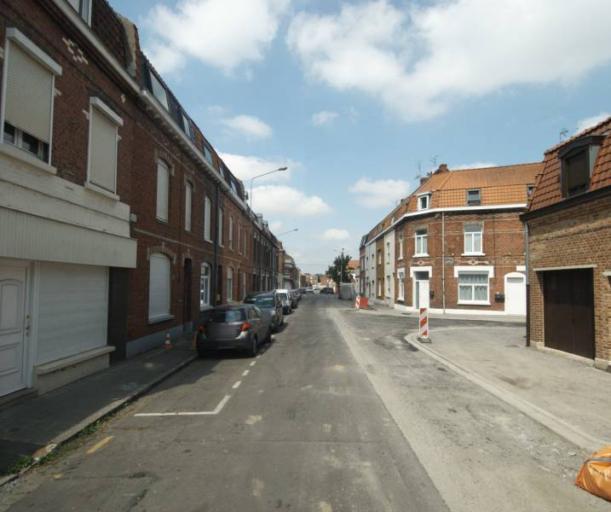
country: FR
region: Nord-Pas-de-Calais
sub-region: Departement du Nord
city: Armentieres
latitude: 50.6914
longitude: 2.8754
